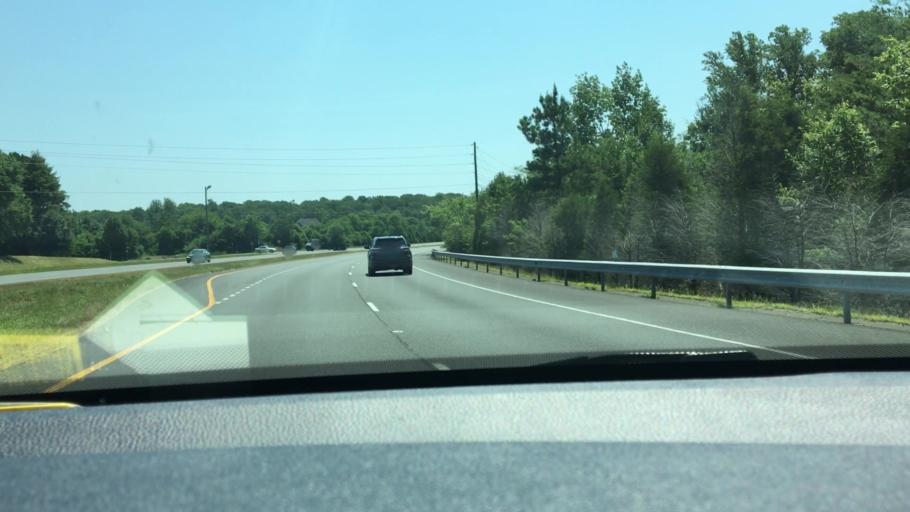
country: US
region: Virginia
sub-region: Prince William County
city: Buckhall
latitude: 38.7345
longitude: -77.4300
